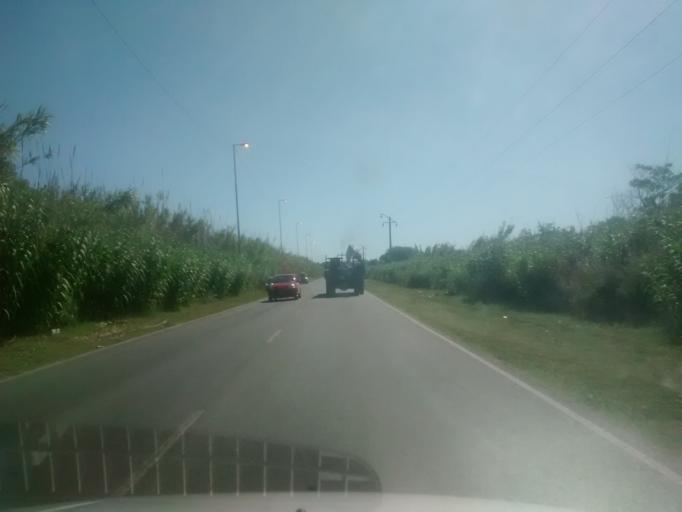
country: AR
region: Buenos Aires
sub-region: Partido de Berisso
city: Berisso
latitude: -34.9079
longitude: -57.9099
